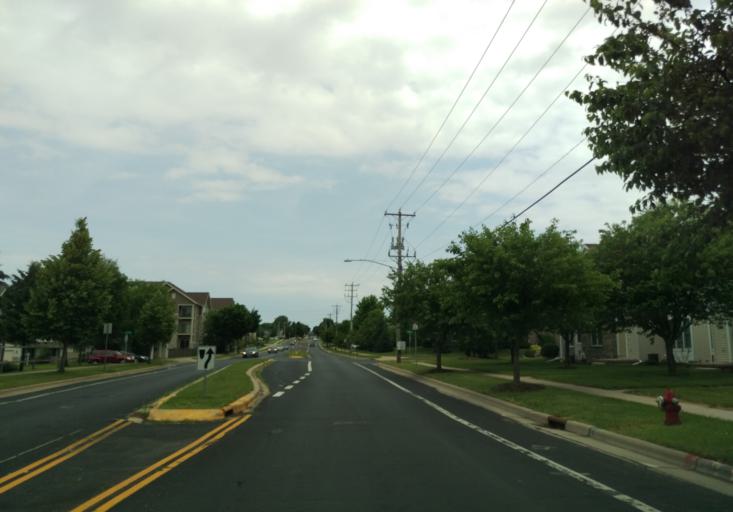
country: US
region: Wisconsin
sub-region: Dane County
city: Verona
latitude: 43.0120
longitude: -89.4989
